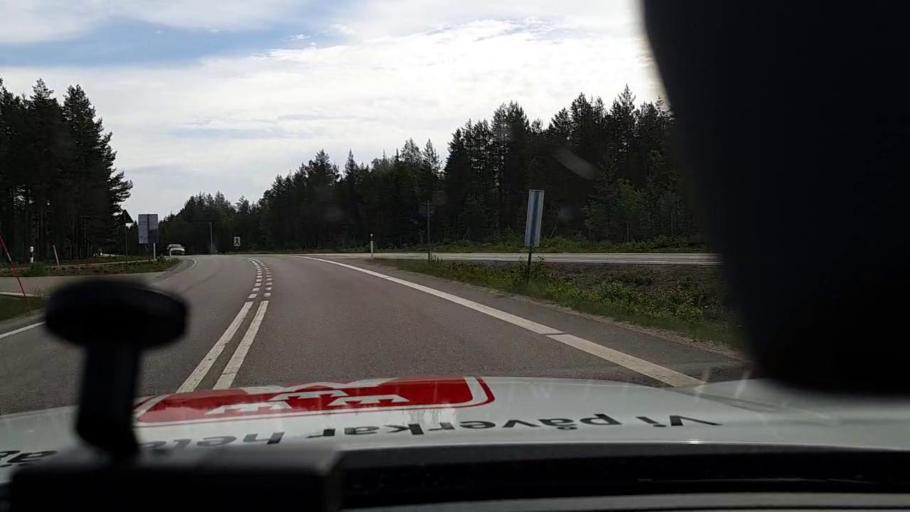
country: SE
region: Norrbotten
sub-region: Lulea Kommun
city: Gammelstad
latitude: 65.5825
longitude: 21.9979
